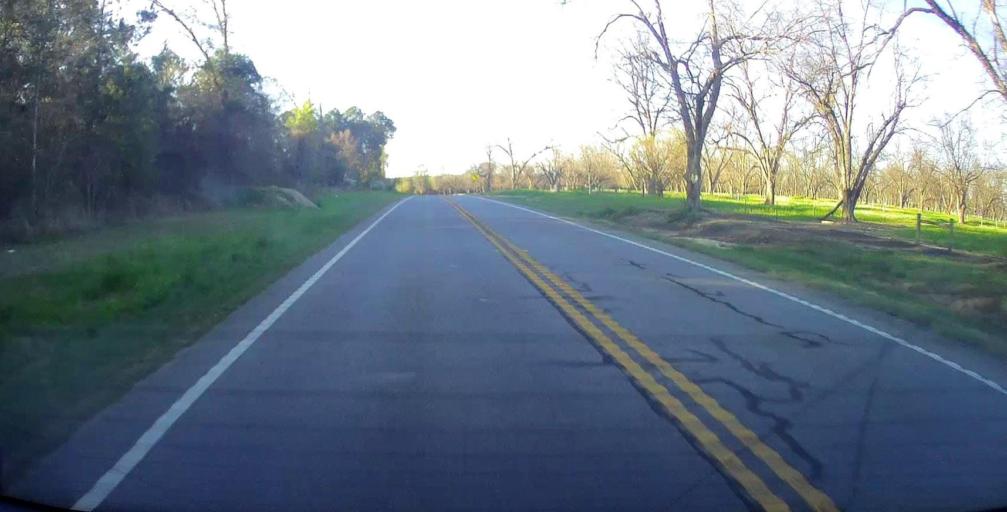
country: US
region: Georgia
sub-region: Wilcox County
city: Abbeville
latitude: 32.0320
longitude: -83.2517
